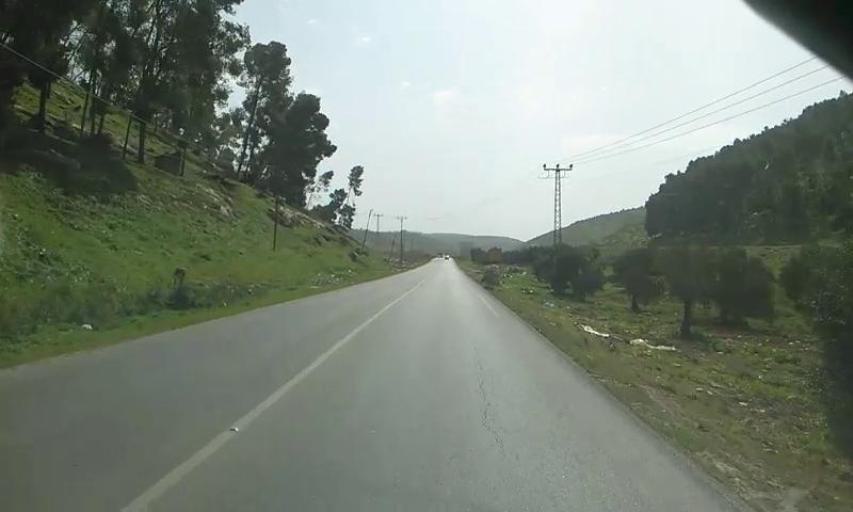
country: PS
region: West Bank
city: Mirkah
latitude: 32.3997
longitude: 35.2243
